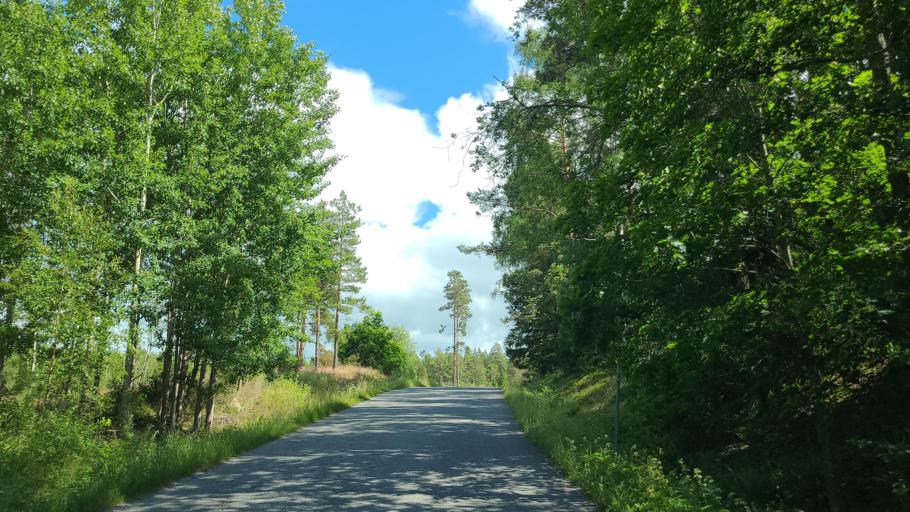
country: FI
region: Varsinais-Suomi
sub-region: Aboland-Turunmaa
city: Nagu
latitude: 60.1753
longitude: 22.0380
